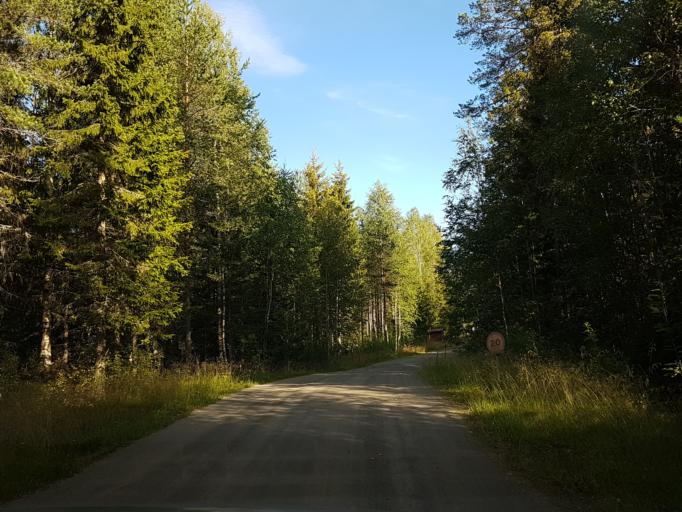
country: SE
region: Vaesterbotten
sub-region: Robertsfors Kommun
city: Robertsfors
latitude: 64.0480
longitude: 20.8921
